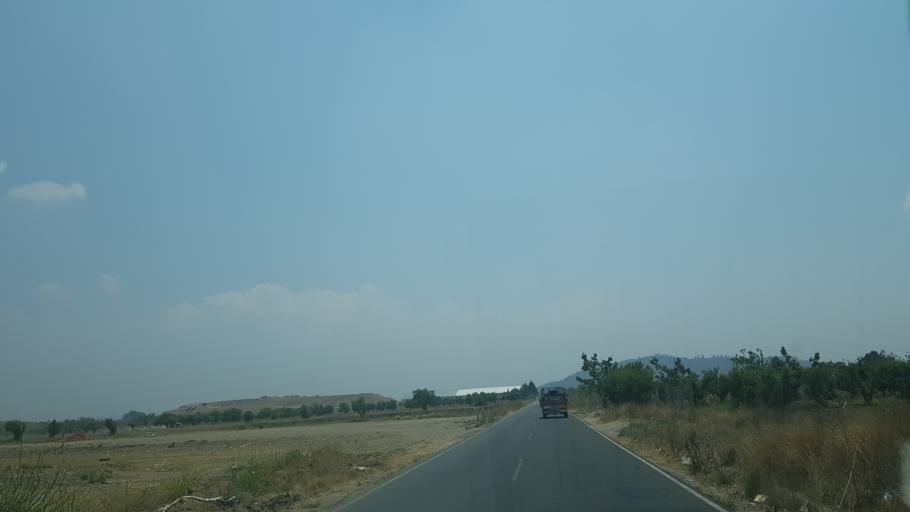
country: MX
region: Puebla
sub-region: San Jeronimo Tecuanipan
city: San Miguel Papaxtla
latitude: 19.0914
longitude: -98.3884
